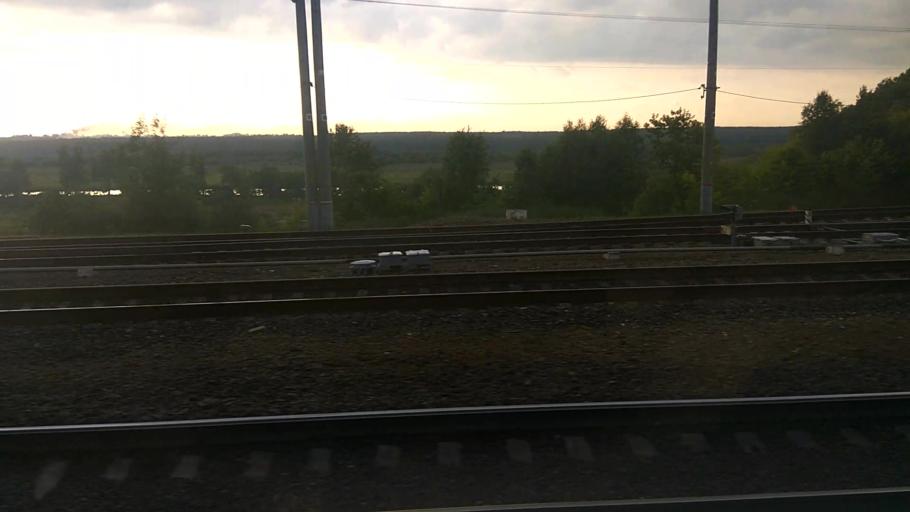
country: RU
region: Moskovskaya
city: Kashira
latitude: 54.8571
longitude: 38.1855
